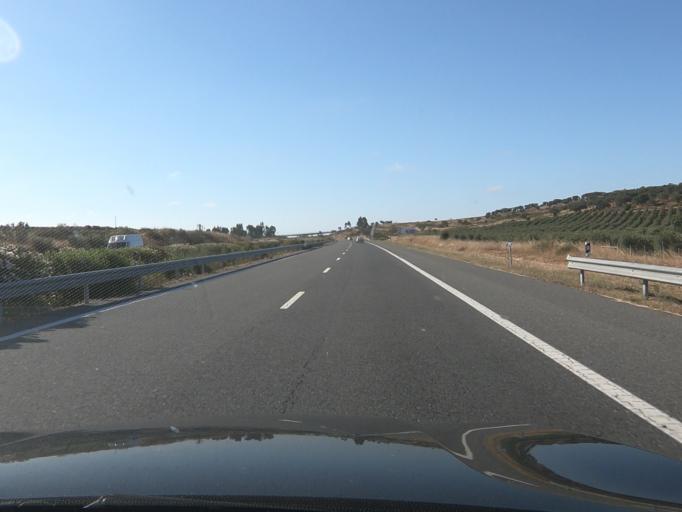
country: PT
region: Beja
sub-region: Ourique
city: Ourique
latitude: 37.7199
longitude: -8.1960
